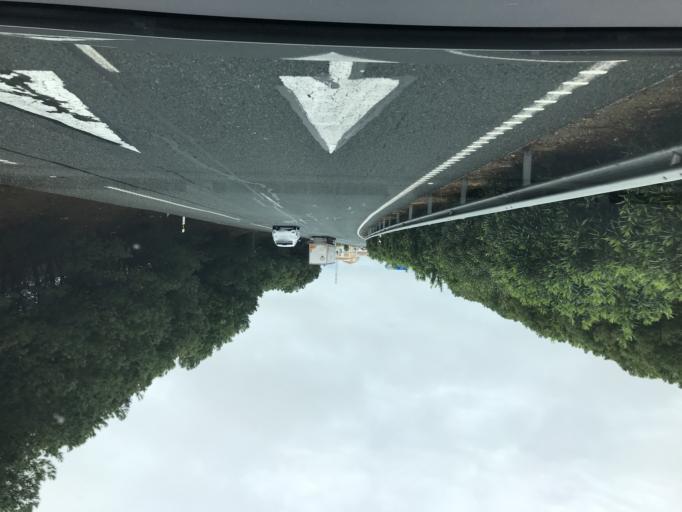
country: ES
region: Andalusia
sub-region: Provincia de Sevilla
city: El Arahal
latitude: 37.2510
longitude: -5.5570
